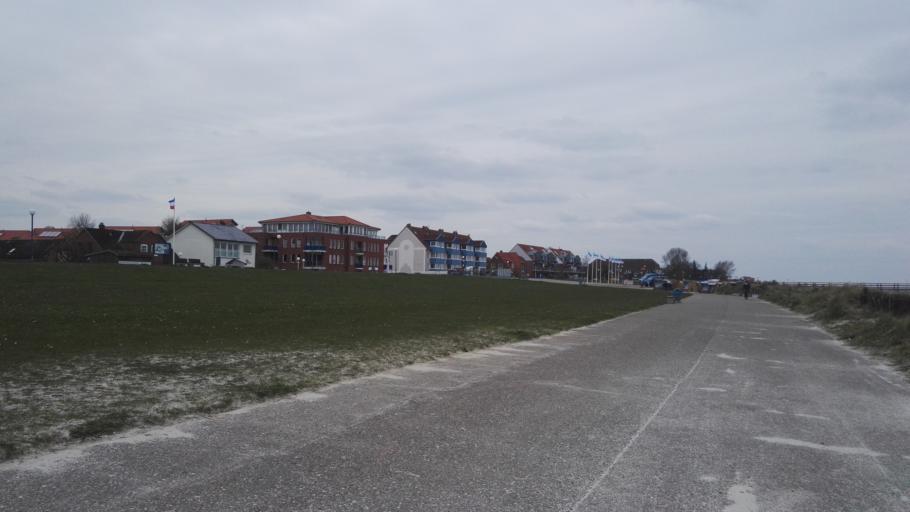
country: DE
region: Schleswig-Holstein
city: Krummbek
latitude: 54.4139
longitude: 10.4161
